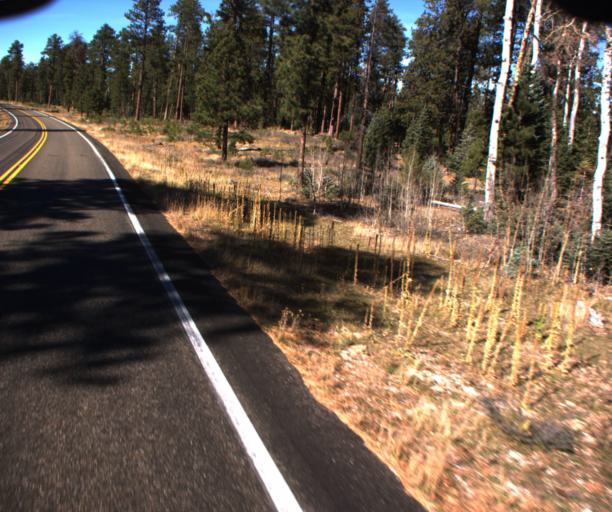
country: US
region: Arizona
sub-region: Coconino County
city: Fredonia
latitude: 36.6434
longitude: -112.1766
